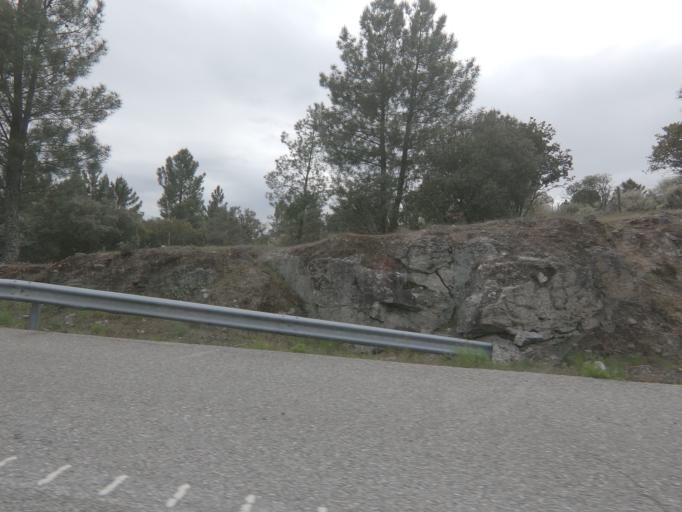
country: PT
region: Guarda
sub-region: Celorico da Beira
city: Celorico da Beira
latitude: 40.6240
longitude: -7.3057
